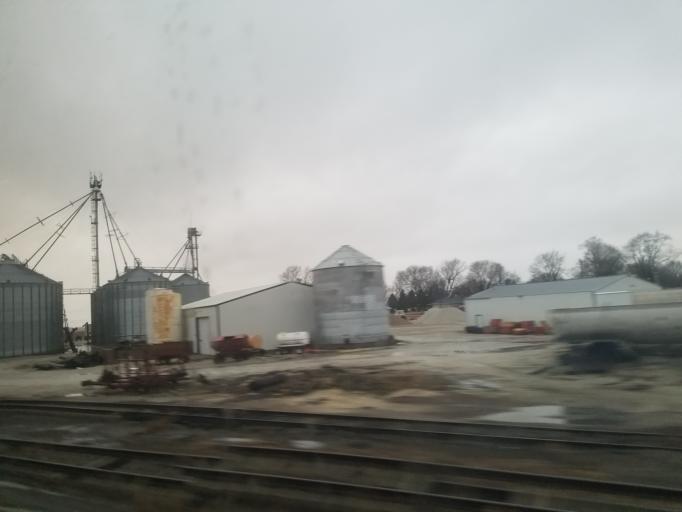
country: US
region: Illinois
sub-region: Warren County
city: Monmouth
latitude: 40.8683
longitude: -90.7511
